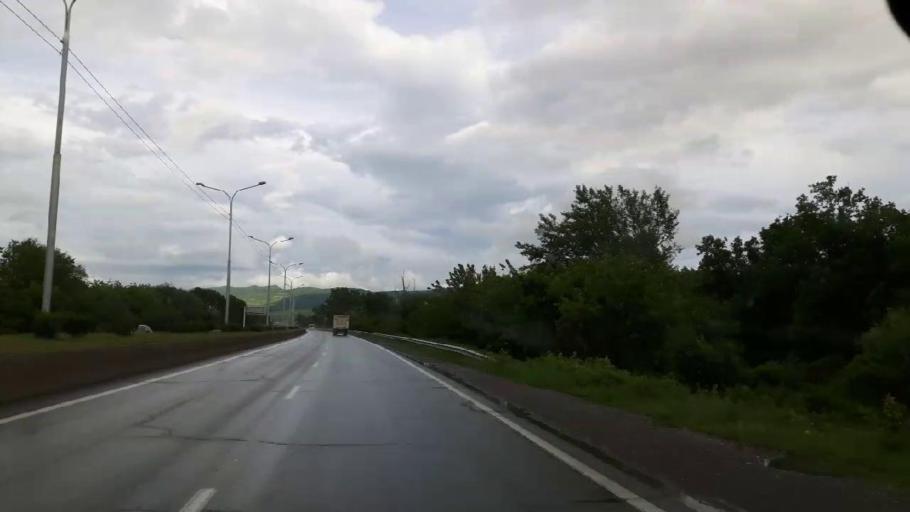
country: GE
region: Shida Kartli
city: Kaspi
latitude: 41.9112
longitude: 44.5658
